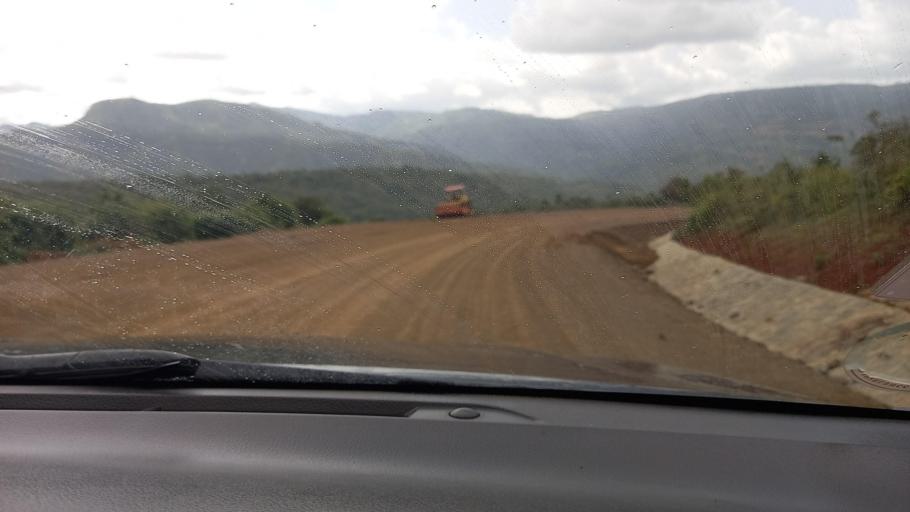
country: ET
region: Southern Nations, Nationalities, and People's Region
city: Mizan Teferi
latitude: 6.1809
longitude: 35.6966
